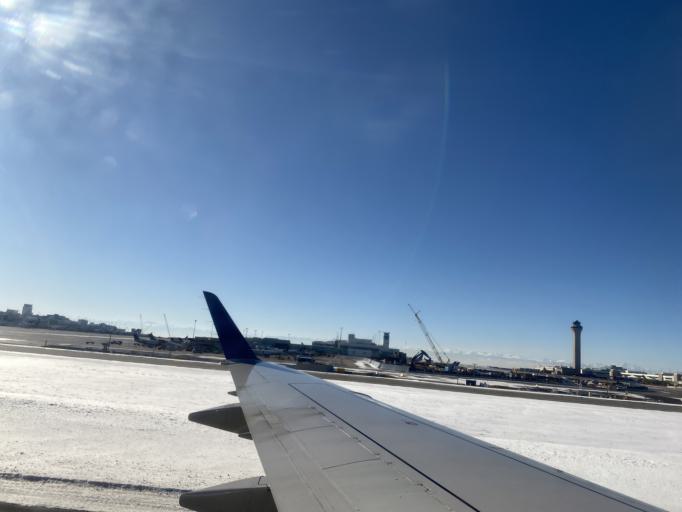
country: US
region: Colorado
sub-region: Weld County
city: Lochbuie
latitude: 39.8583
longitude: -104.6623
